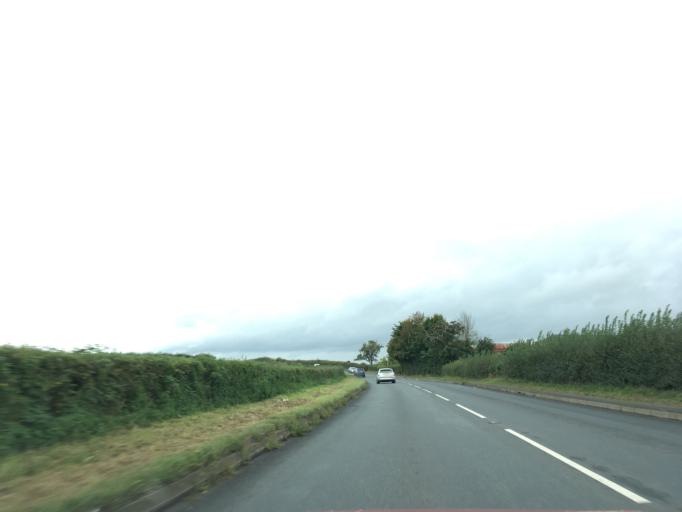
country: GB
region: England
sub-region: Herefordshire
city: Ross on Wye
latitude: 51.9110
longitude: -2.5475
